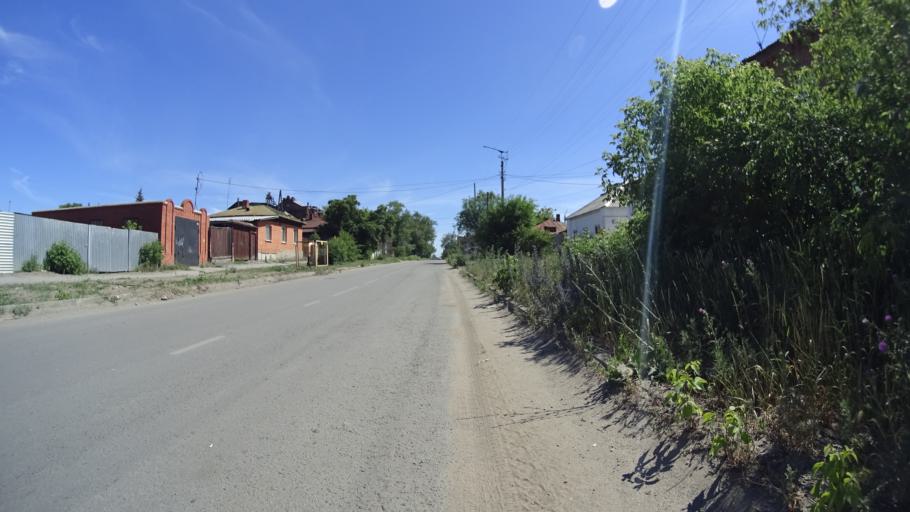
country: RU
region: Chelyabinsk
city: Troitsk
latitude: 54.0897
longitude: 61.5518
